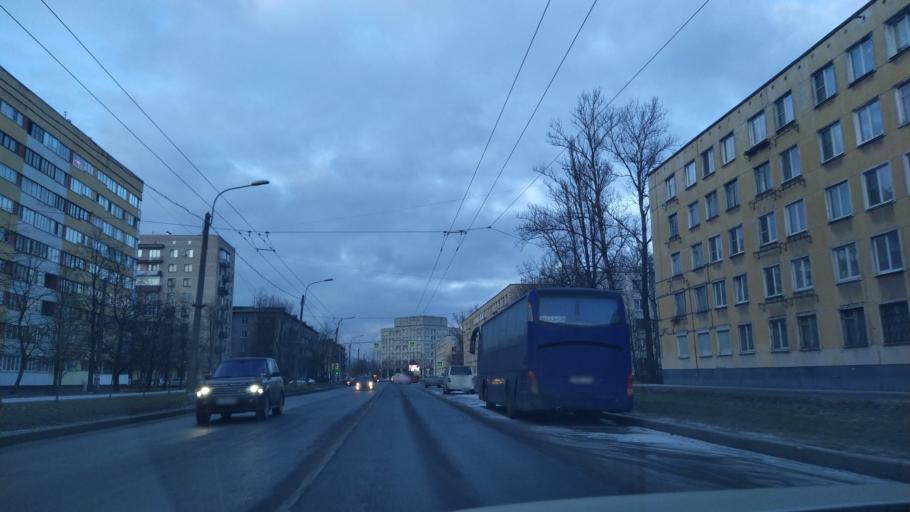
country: RU
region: St.-Petersburg
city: Dachnoye
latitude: 59.8539
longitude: 30.2563
